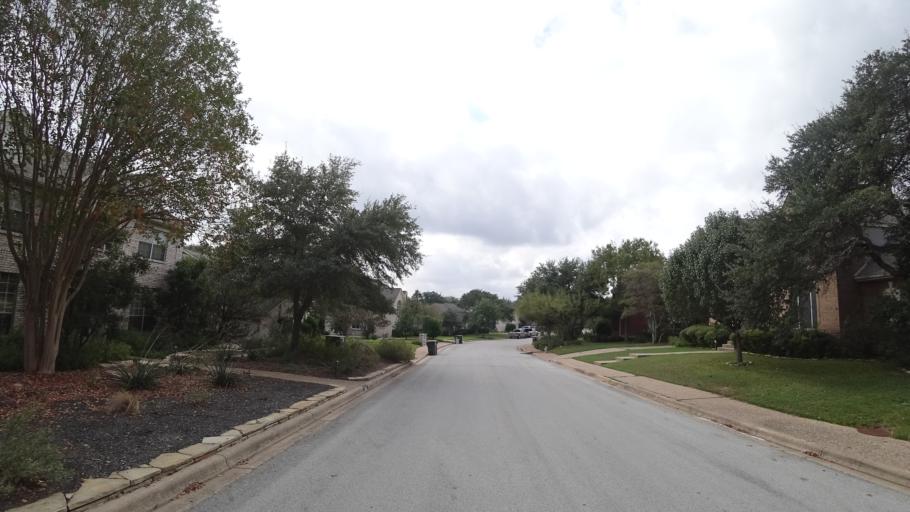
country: US
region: Texas
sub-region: Travis County
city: Barton Creek
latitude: 30.2949
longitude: -97.8958
